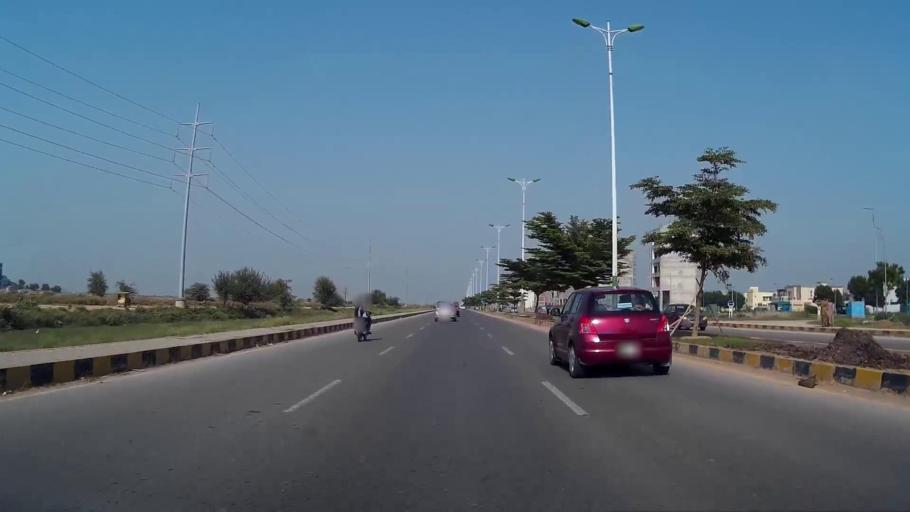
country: PK
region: Punjab
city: Lahore
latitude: 31.4747
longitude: 74.4439
